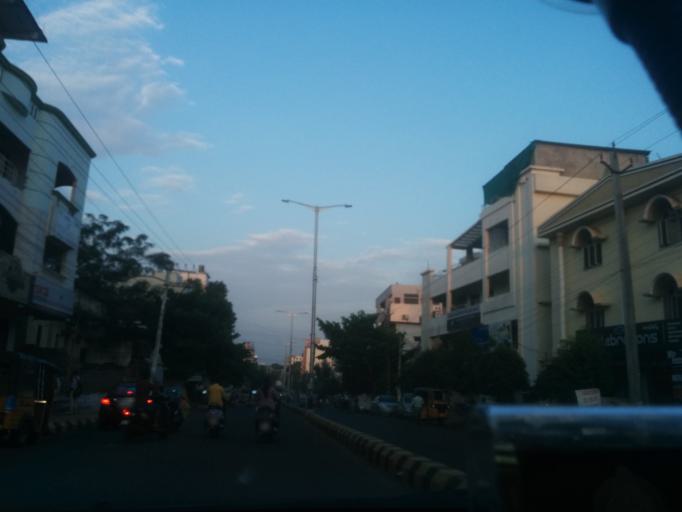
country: IN
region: Andhra Pradesh
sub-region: East Godavari
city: Rajahmundry
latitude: 17.0075
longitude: 81.7955
